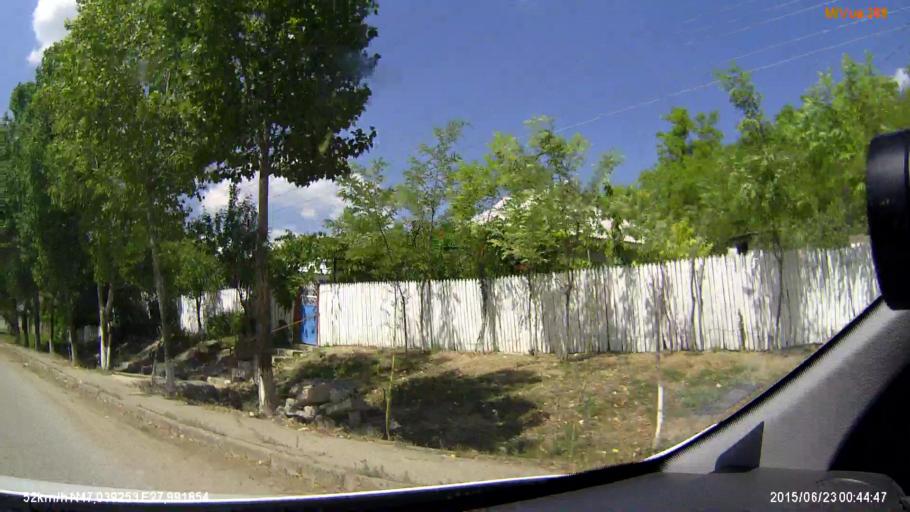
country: RO
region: Iasi
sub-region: Comuna Grozesti
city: Grozesti
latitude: 47.0392
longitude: 27.9920
